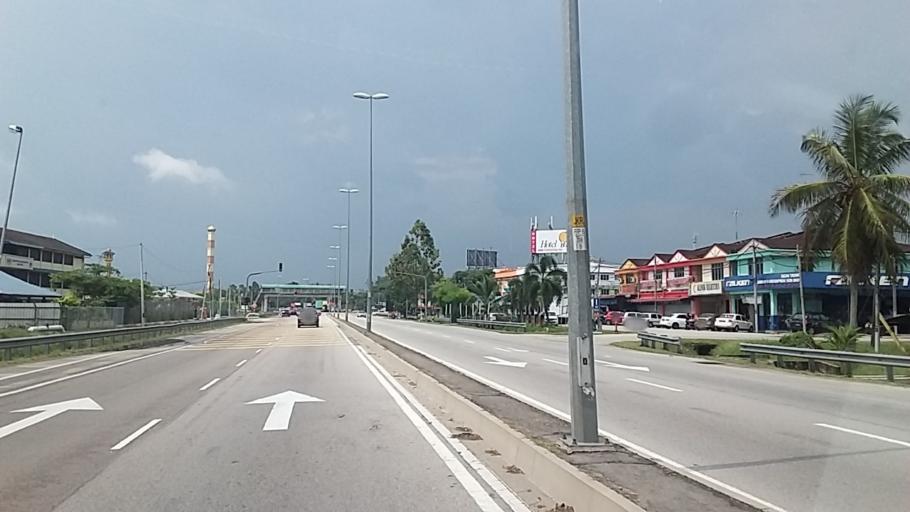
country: MY
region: Johor
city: Parit Raja
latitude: 1.8563
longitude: 103.0971
